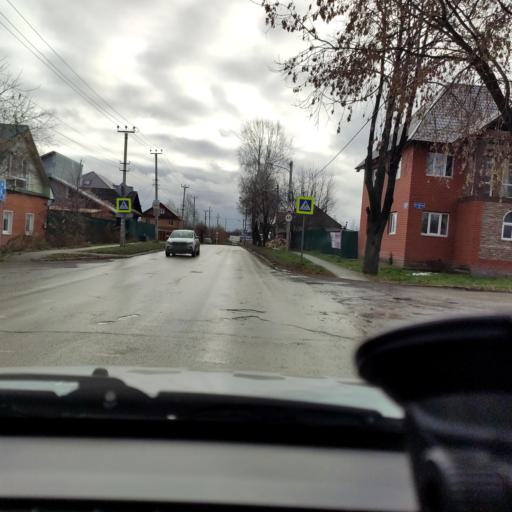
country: RU
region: Perm
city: Perm
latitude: 58.0236
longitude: 56.3355
